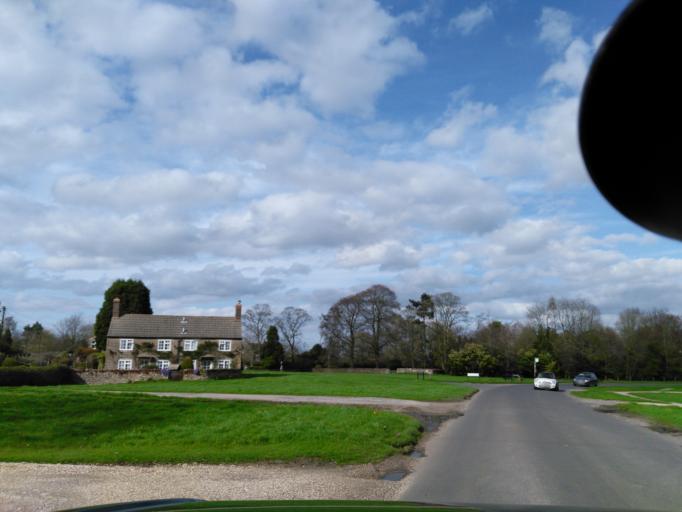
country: GB
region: England
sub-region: Wiltshire
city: Chippenham
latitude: 51.4903
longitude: -2.1139
